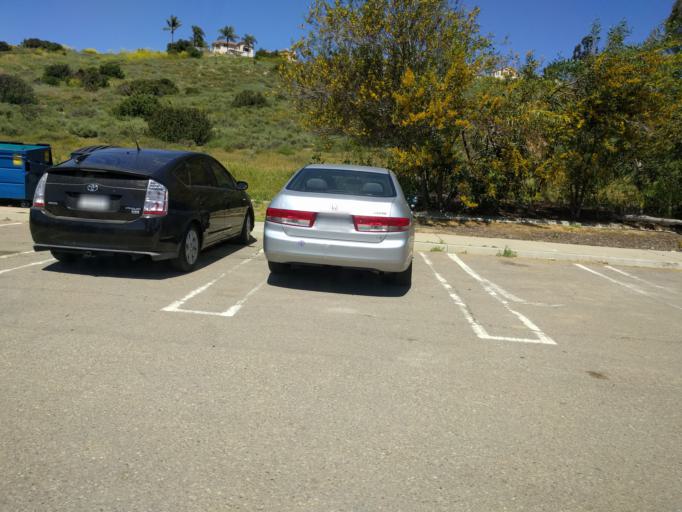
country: US
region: California
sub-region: San Diego County
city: Fairbanks Ranch
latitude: 32.9422
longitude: -117.1340
